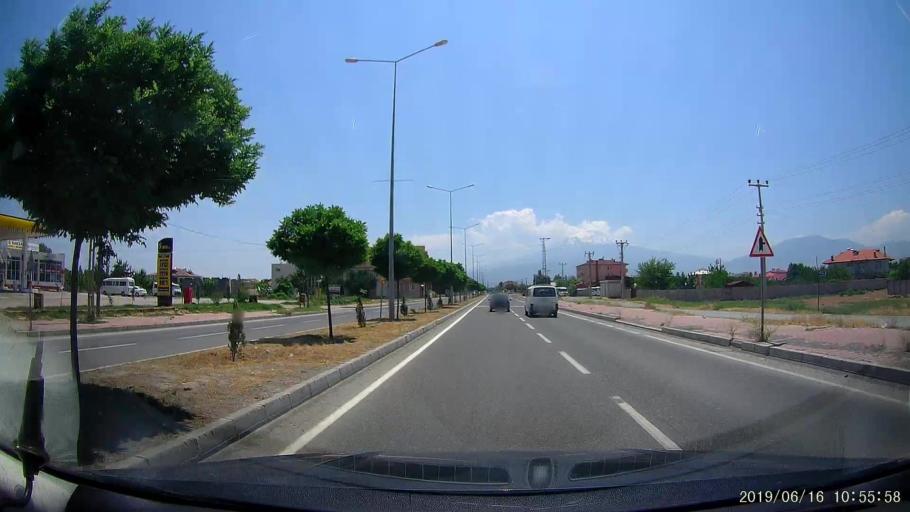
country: TR
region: Igdir
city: Igdir
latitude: 39.9331
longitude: 44.0163
